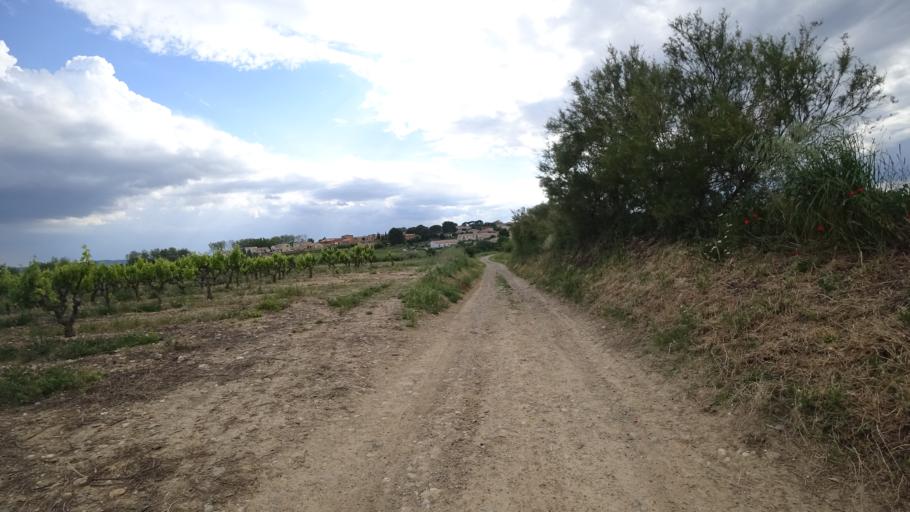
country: FR
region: Languedoc-Roussillon
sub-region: Departement de l'Aude
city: Ginestas
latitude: 43.2506
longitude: 2.8676
